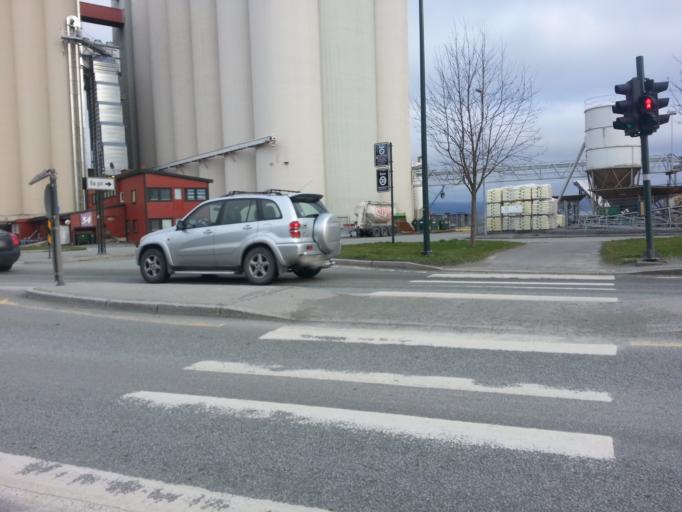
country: NO
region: Sor-Trondelag
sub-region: Trondheim
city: Trondheim
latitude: 63.4316
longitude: 10.3679
